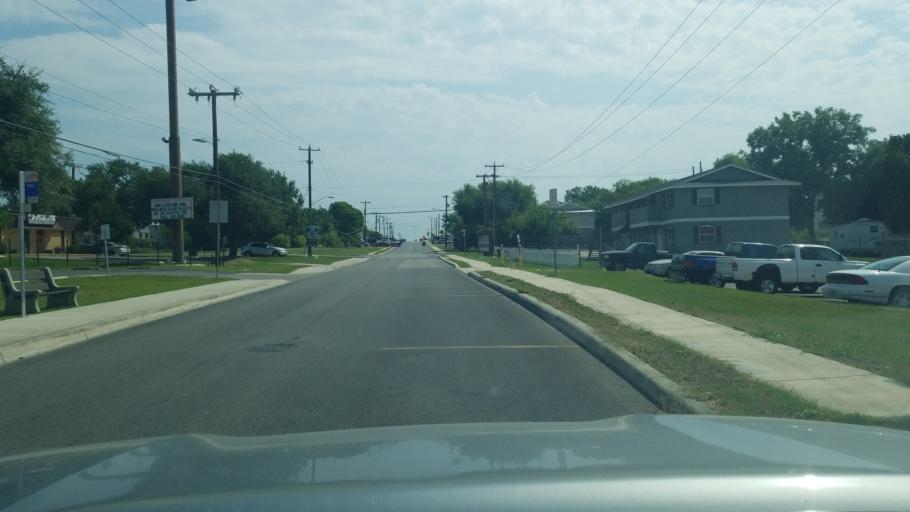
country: US
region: Texas
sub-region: Bexar County
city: Castle Hills
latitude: 29.5401
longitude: -98.5265
